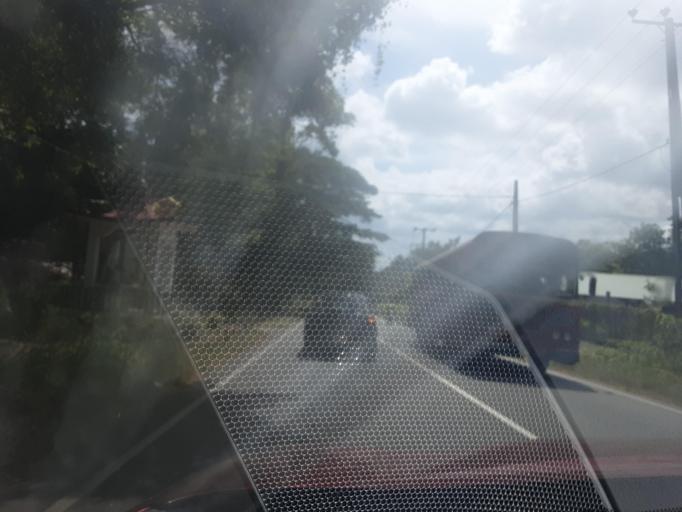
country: LK
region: North Western
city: Kuliyapitiya
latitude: 7.4840
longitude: 79.9768
